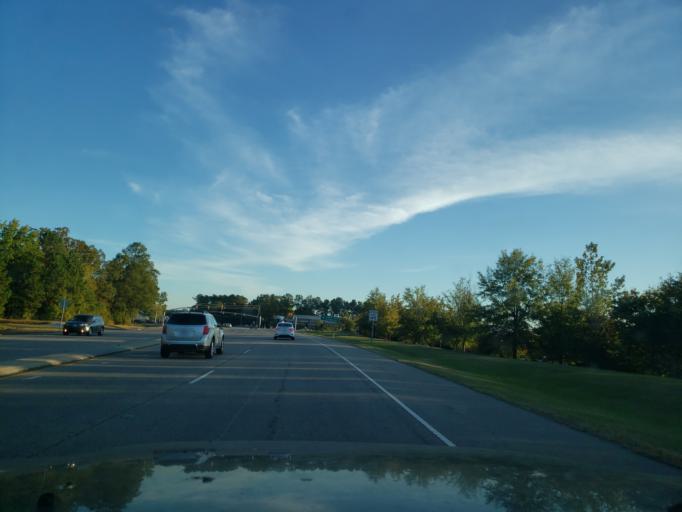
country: US
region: North Carolina
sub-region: Wake County
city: Morrisville
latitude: 35.8365
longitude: -78.8560
